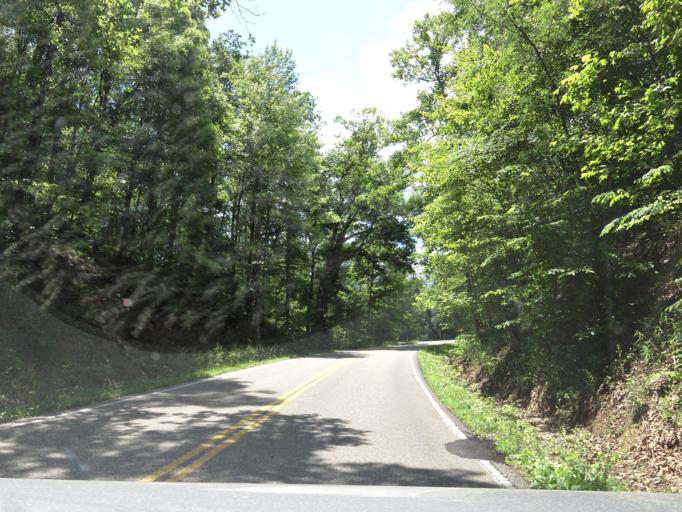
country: US
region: Tennessee
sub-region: Loudon County
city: Greenback
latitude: 35.5136
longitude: -83.9884
